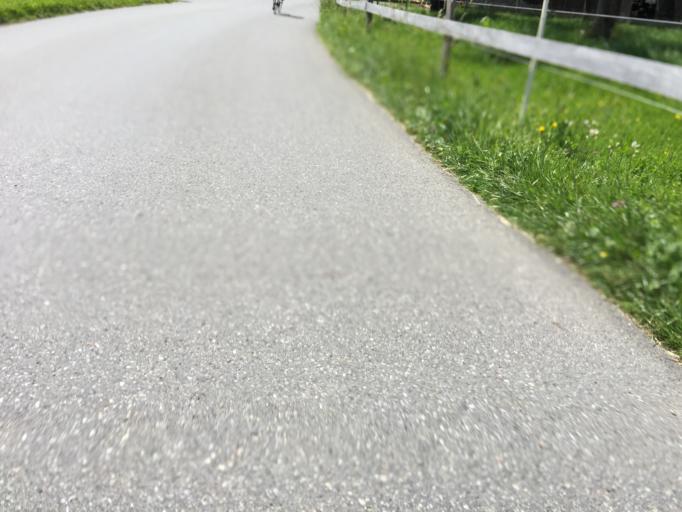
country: CH
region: Bern
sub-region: Bern-Mittelland District
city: Konolfingen
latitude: 46.8791
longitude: 7.6053
